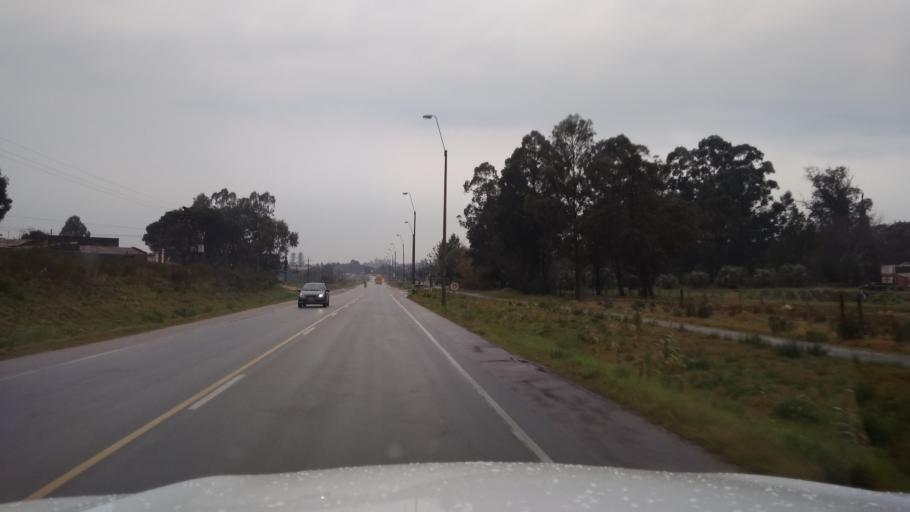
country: UY
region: Canelones
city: Toledo
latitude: -34.7606
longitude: -56.1155
